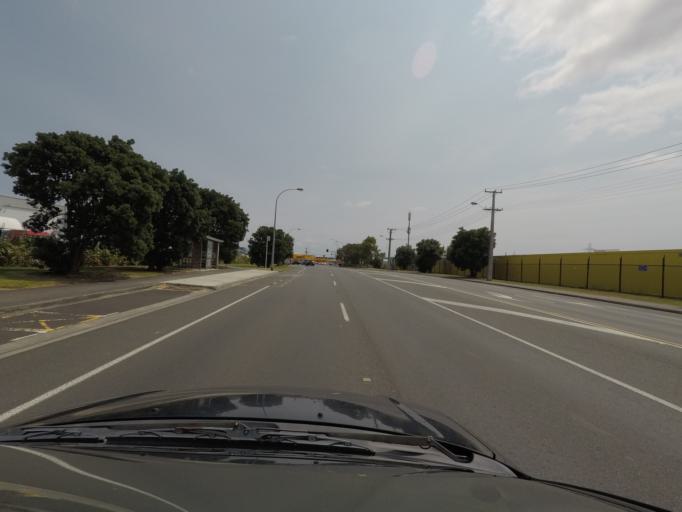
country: NZ
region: Auckland
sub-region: Auckland
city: Waitakere
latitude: -36.9117
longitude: 174.6897
